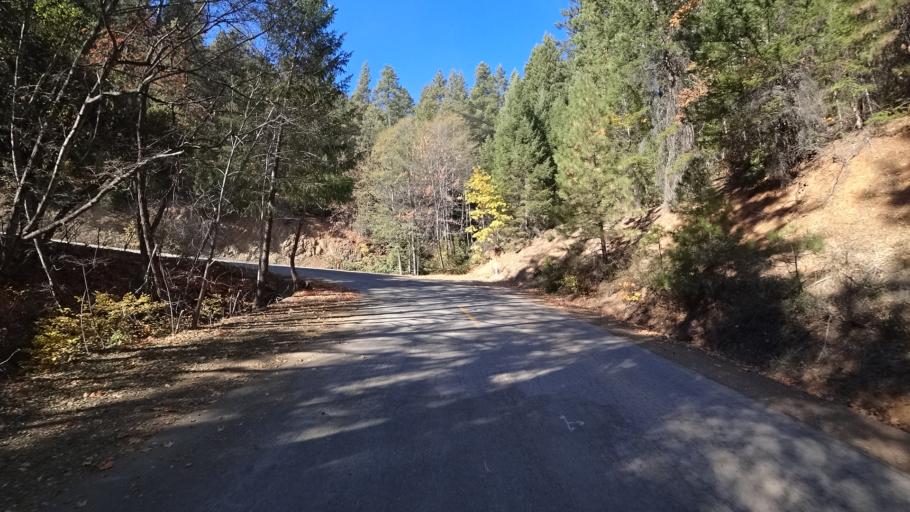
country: US
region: California
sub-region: Siskiyou County
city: Yreka
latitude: 41.7316
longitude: -122.7271
